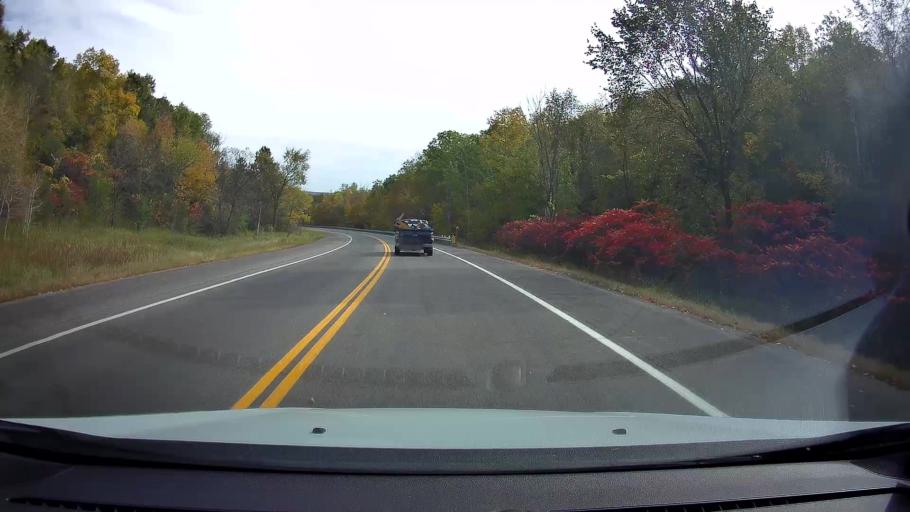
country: US
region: Wisconsin
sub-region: Polk County
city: Osceola
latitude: 45.3199
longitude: -92.7254
